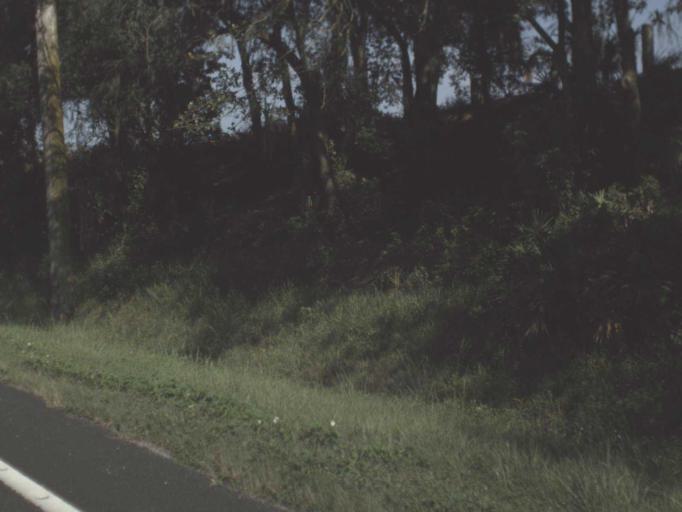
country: US
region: Florida
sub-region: Hillsborough County
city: Valrico
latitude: 27.9378
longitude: -82.1961
